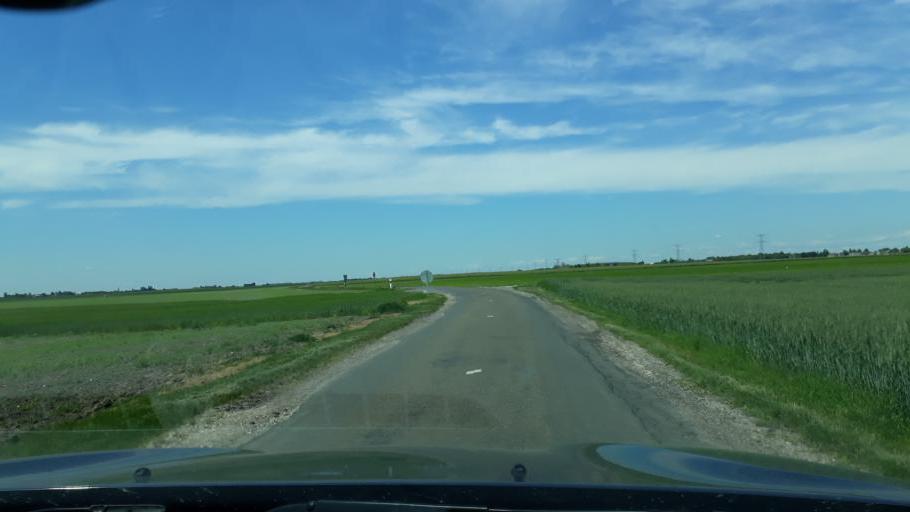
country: FR
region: Centre
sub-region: Departement du Loiret
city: Pithiviers
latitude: 48.1073
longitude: 2.2378
